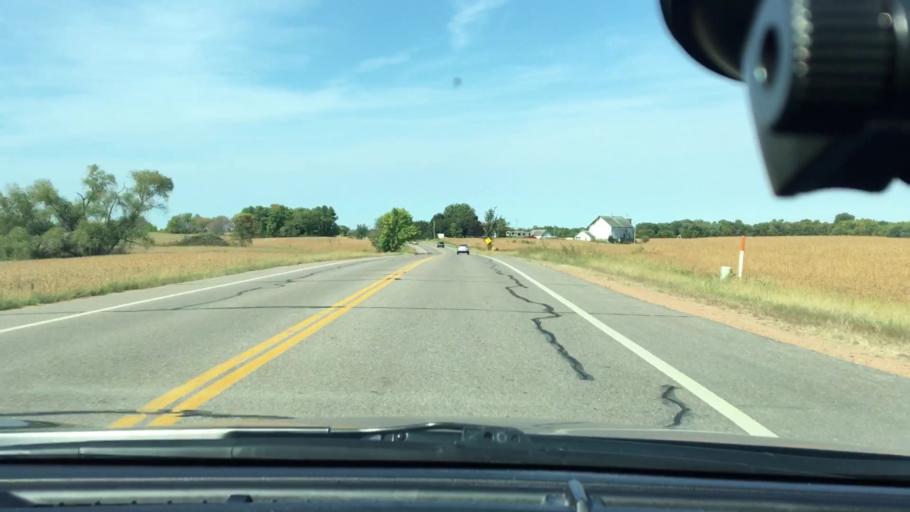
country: US
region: Minnesota
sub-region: Hennepin County
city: Corcoran
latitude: 45.0892
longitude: -93.5330
